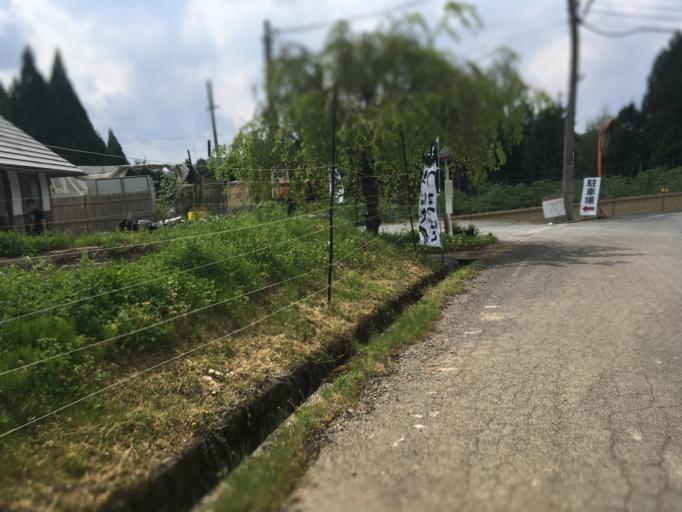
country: JP
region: Kyoto
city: Kameoka
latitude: 35.0897
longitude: 135.6090
